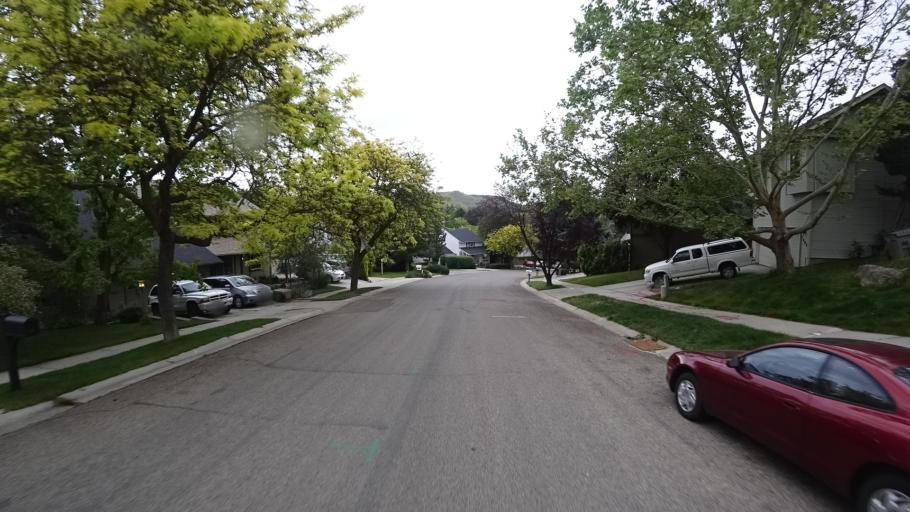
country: US
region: Idaho
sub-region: Ada County
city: Boise
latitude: 43.6138
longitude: -116.1702
